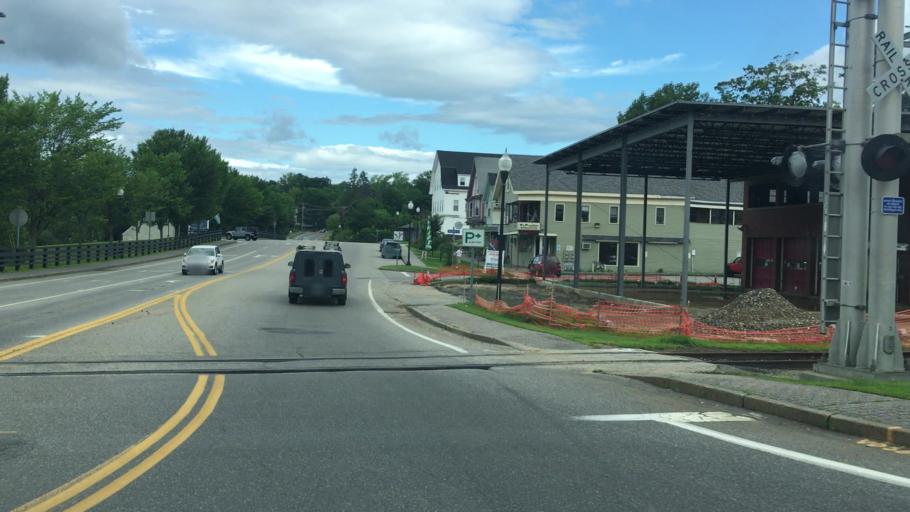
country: US
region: New Hampshire
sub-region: Belknap County
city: Laconia
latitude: 43.5475
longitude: -71.4627
